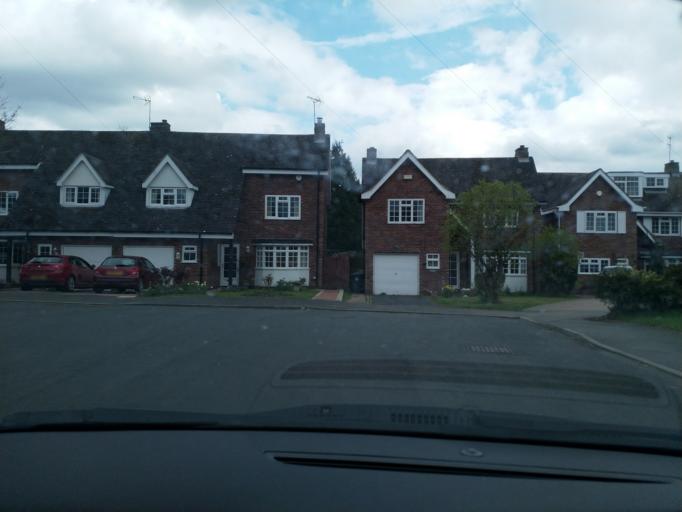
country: GB
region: England
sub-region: Warwickshire
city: Henley in Arden
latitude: 52.2827
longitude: -1.7158
